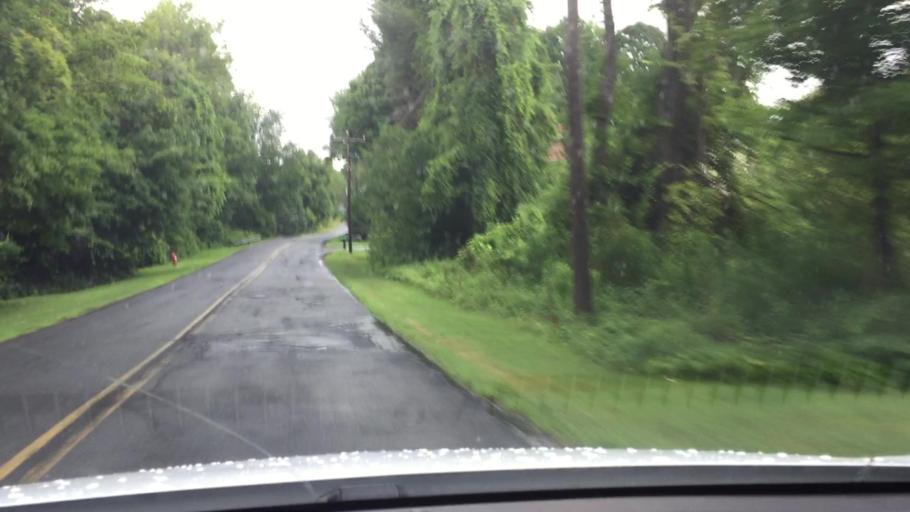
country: US
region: Massachusetts
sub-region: Berkshire County
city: Dalton
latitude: 42.4245
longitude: -73.1933
